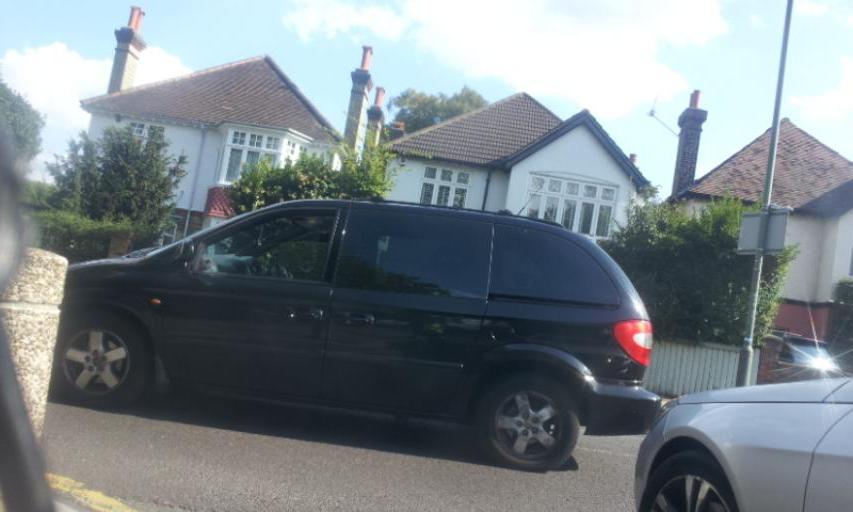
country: GB
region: England
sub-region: Greater London
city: Bromley
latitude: 51.3978
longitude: 0.0136
